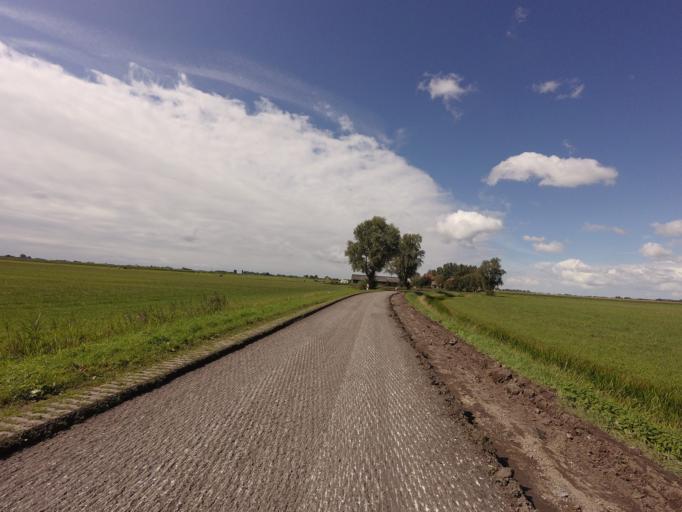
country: NL
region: Friesland
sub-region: Sudwest Fryslan
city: Bolsward
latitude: 53.0299
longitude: 5.5704
